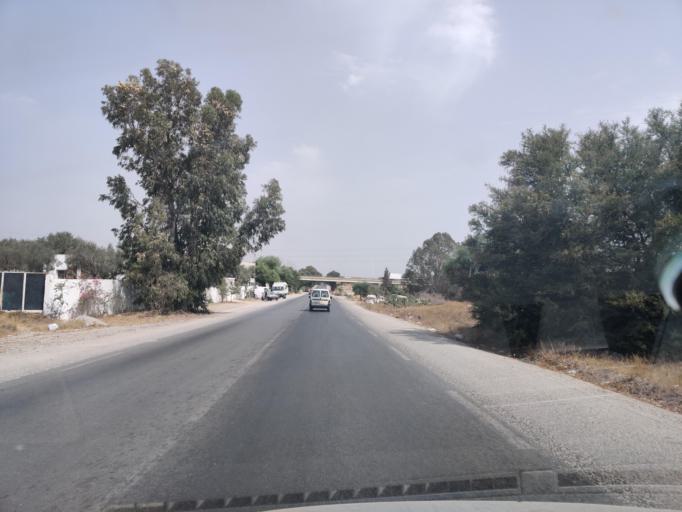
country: TN
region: Nabul
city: Al Hammamat
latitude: 36.4391
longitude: 10.5733
